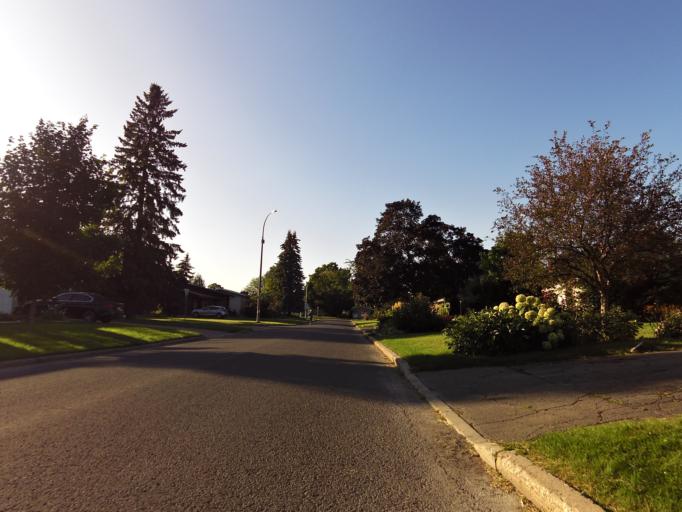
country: CA
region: Ontario
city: Ottawa
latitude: 45.3579
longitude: -75.7231
